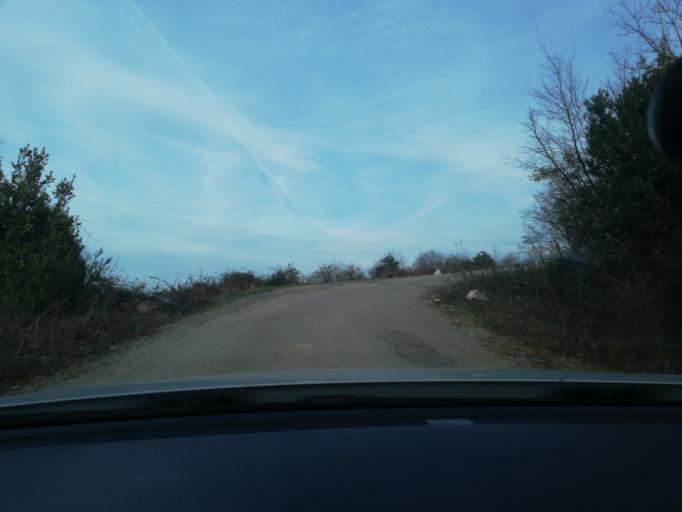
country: TR
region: Zonguldak
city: Tieum
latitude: 41.5492
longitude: 32.0333
